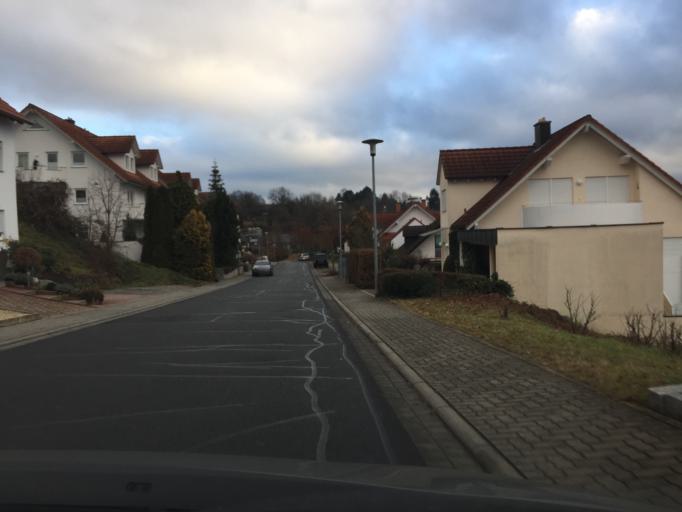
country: DE
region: Bavaria
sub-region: Regierungsbezirk Unterfranken
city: Goldbach
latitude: 50.0015
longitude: 9.1768
